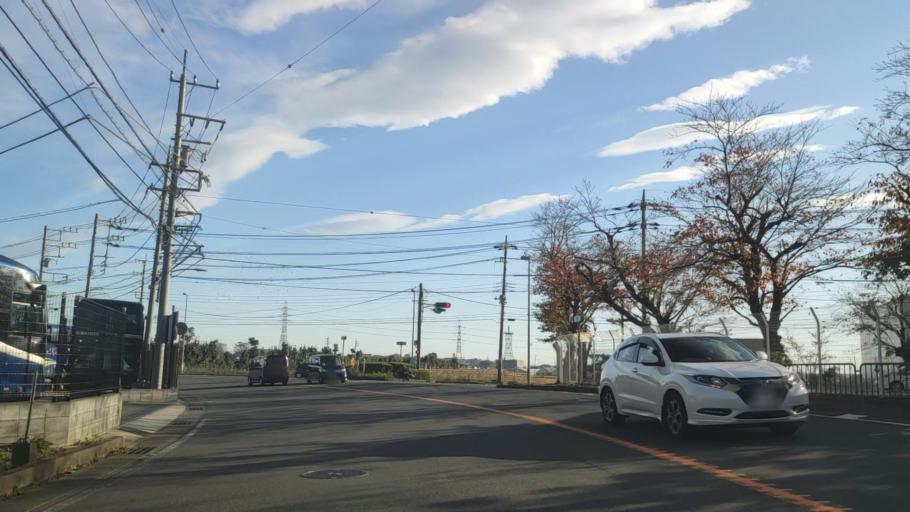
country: JP
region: Kanagawa
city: Atsugi
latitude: 35.4219
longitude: 139.3877
